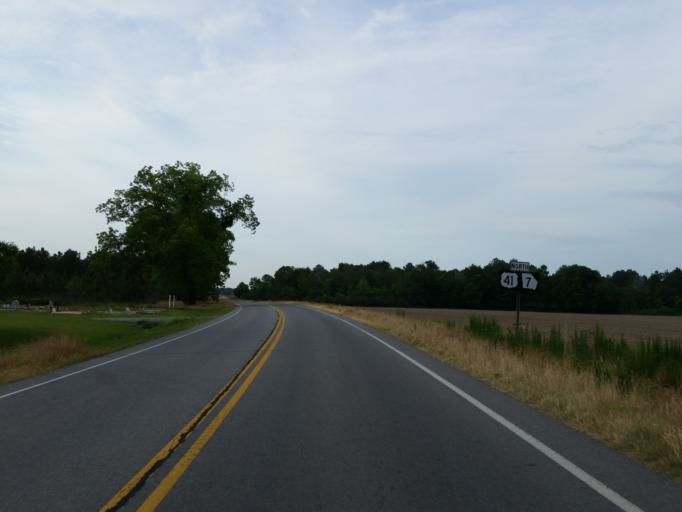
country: US
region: Georgia
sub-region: Dooly County
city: Unadilla
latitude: 32.2065
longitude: -83.7597
